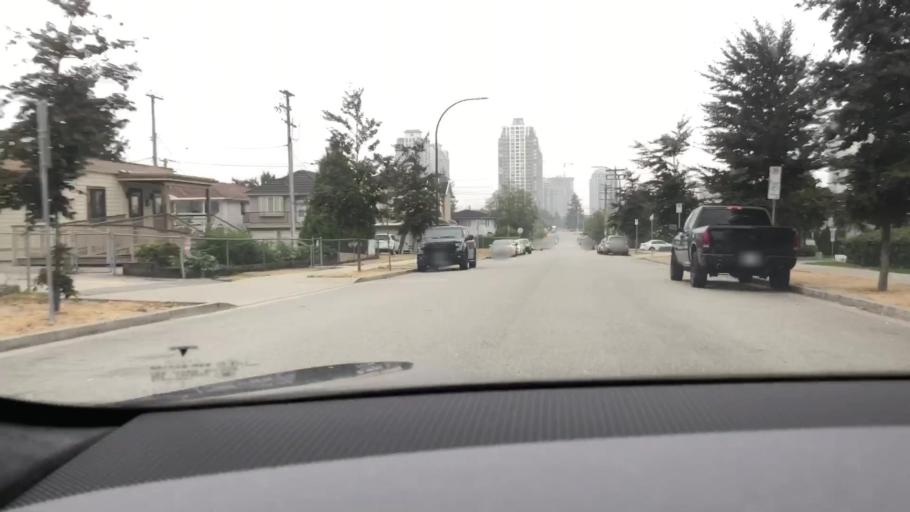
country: CA
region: British Columbia
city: Burnaby
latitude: 49.2197
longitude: -122.9654
